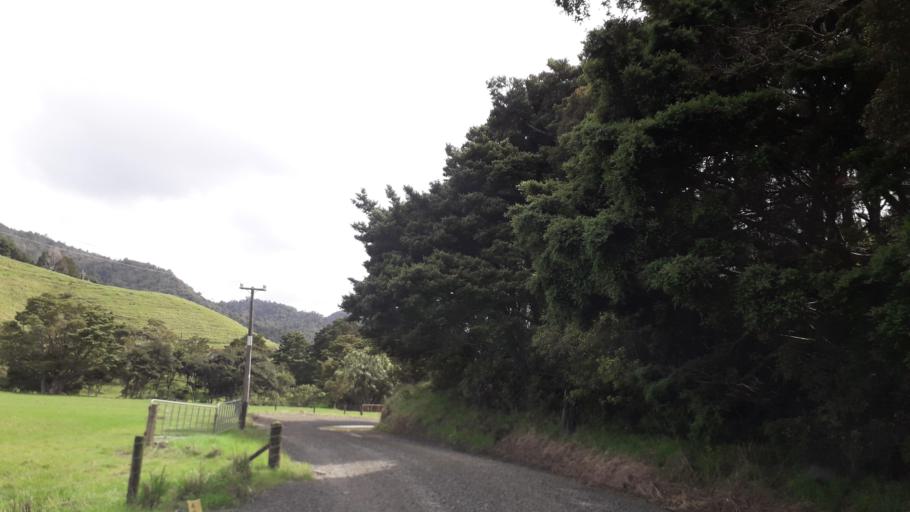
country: NZ
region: Northland
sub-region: Far North District
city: Ahipara
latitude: -35.2351
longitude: 173.2644
